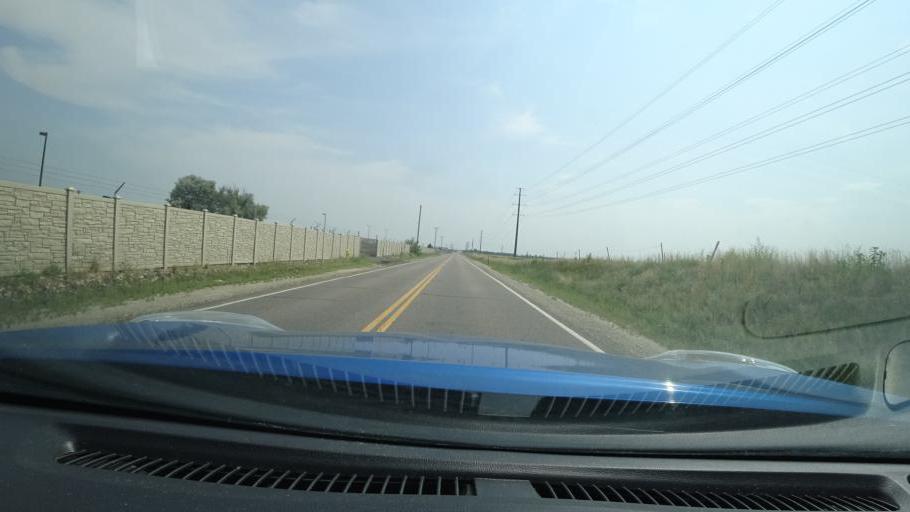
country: US
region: Colorado
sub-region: Adams County
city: Aurora
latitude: 39.7654
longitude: -104.7346
